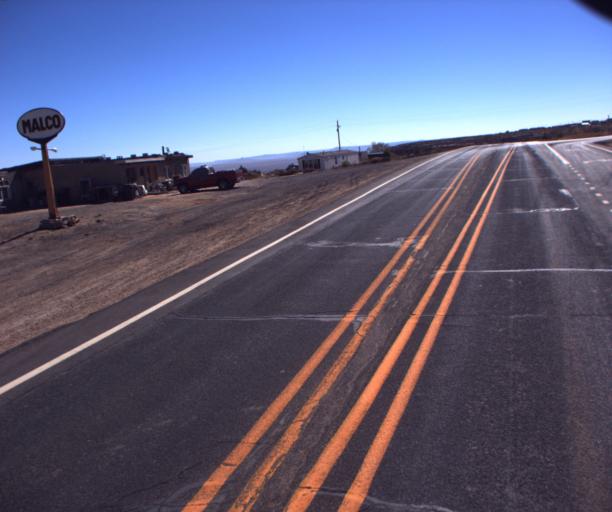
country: US
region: Arizona
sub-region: Navajo County
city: First Mesa
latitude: 35.8175
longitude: -110.5303
